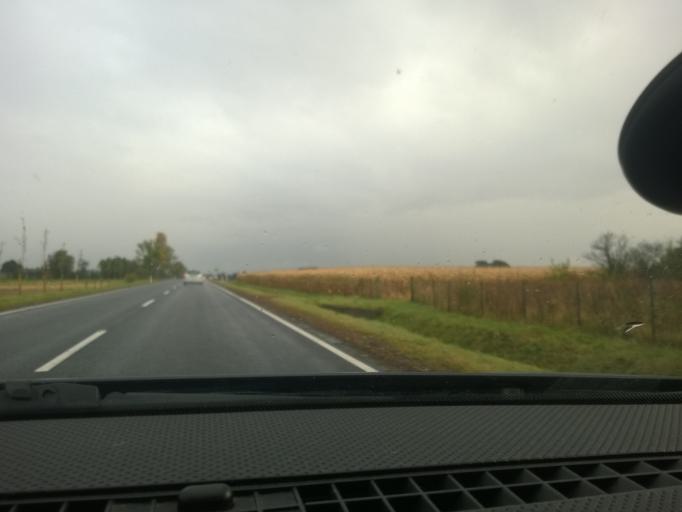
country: PL
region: Lodz Voivodeship
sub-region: Powiat sieradzki
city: Blaszki
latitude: 51.6810
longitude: 18.3419
